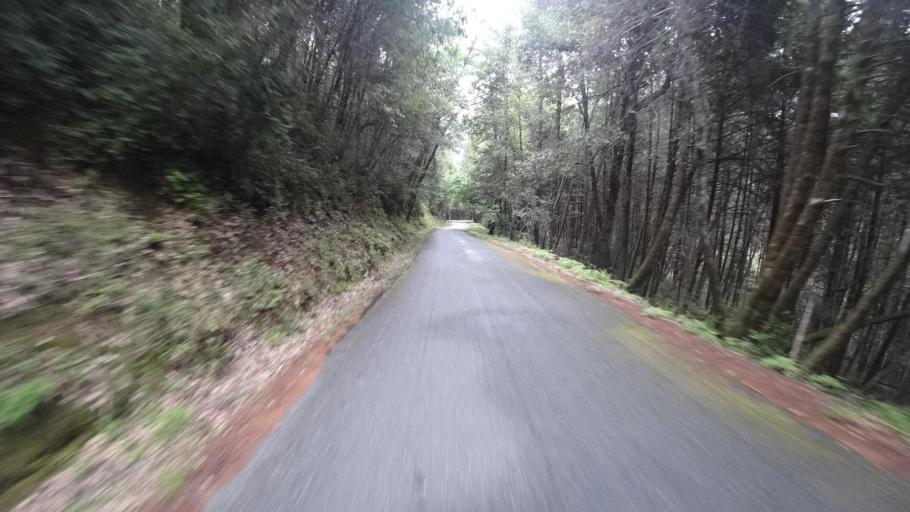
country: US
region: California
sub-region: Humboldt County
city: Willow Creek
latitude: 41.1993
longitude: -123.7561
